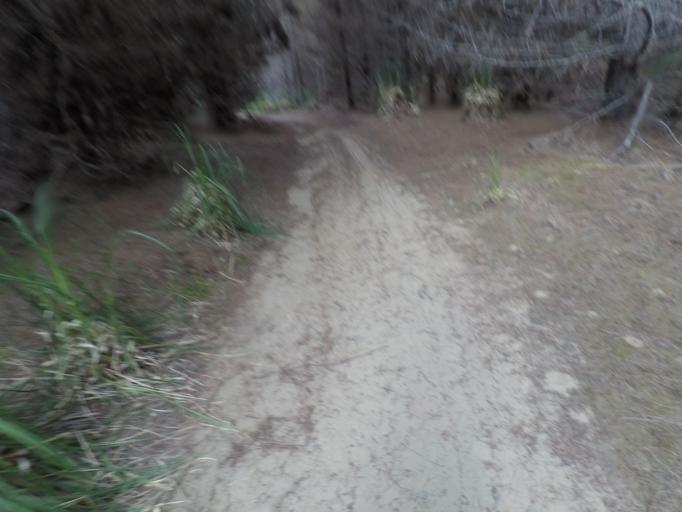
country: NZ
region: Auckland
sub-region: Auckland
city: Parakai
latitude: -36.6010
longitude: 174.2741
